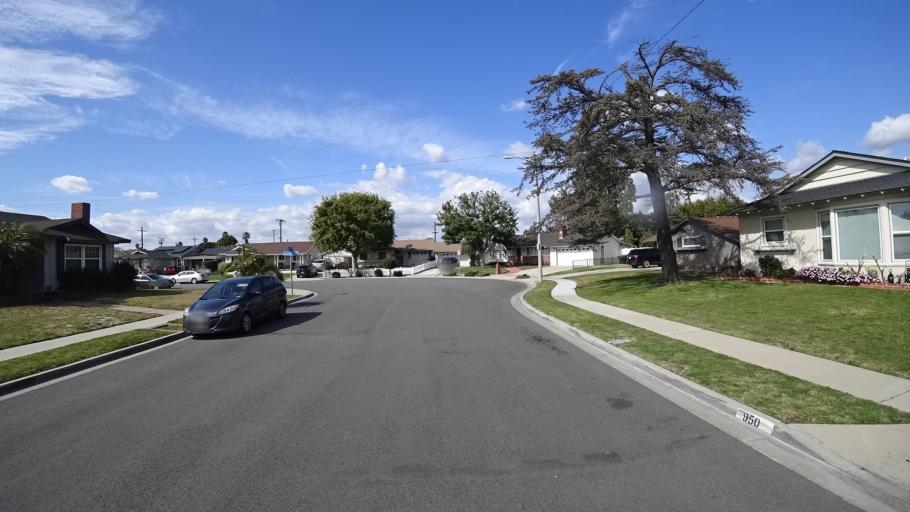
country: US
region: California
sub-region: Orange County
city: Anaheim
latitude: 33.8457
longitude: -117.9287
